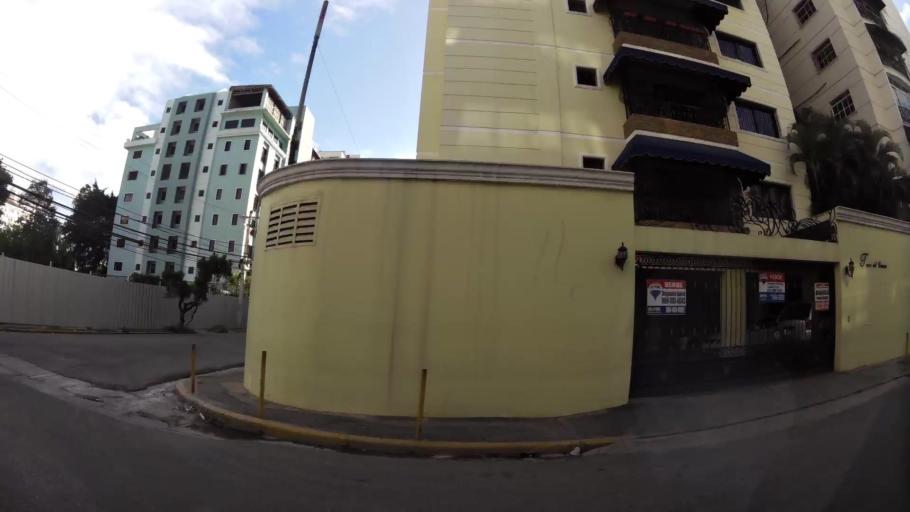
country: DO
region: Nacional
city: La Julia
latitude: 18.4786
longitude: -69.9422
